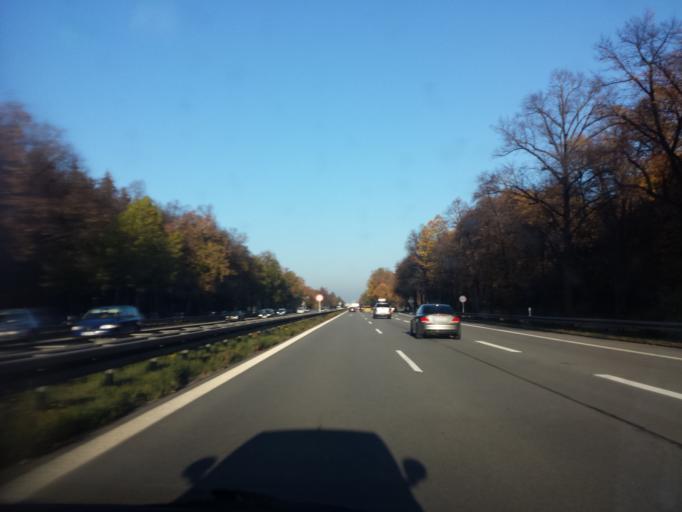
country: DE
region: Bavaria
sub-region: Upper Bavaria
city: Neuried
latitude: 48.1000
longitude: 11.4970
